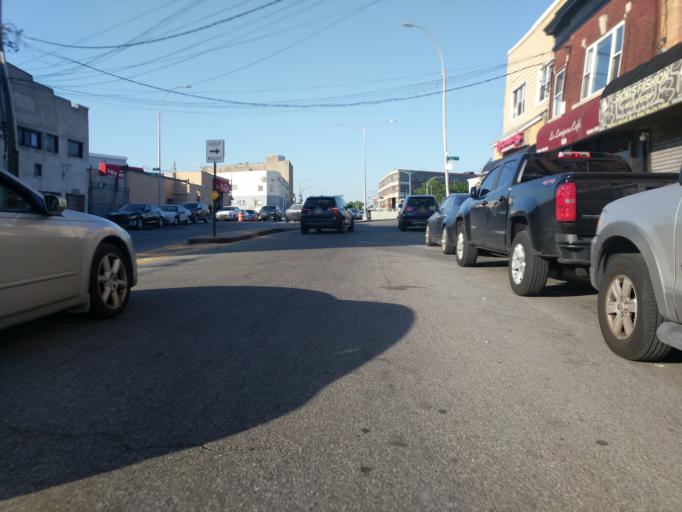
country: US
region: New York
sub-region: Queens County
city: Long Island City
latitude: 40.7151
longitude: -73.9131
